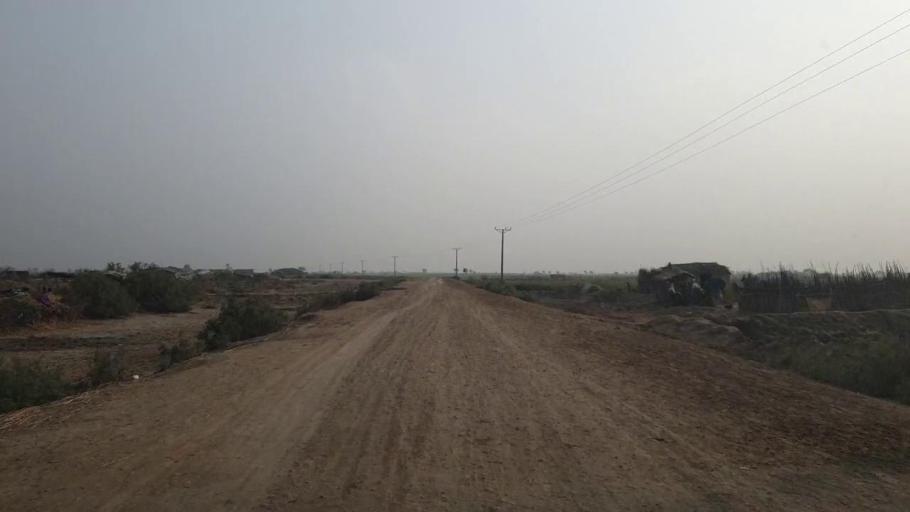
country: PK
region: Sindh
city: Mirpur Batoro
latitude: 24.5548
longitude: 68.4210
